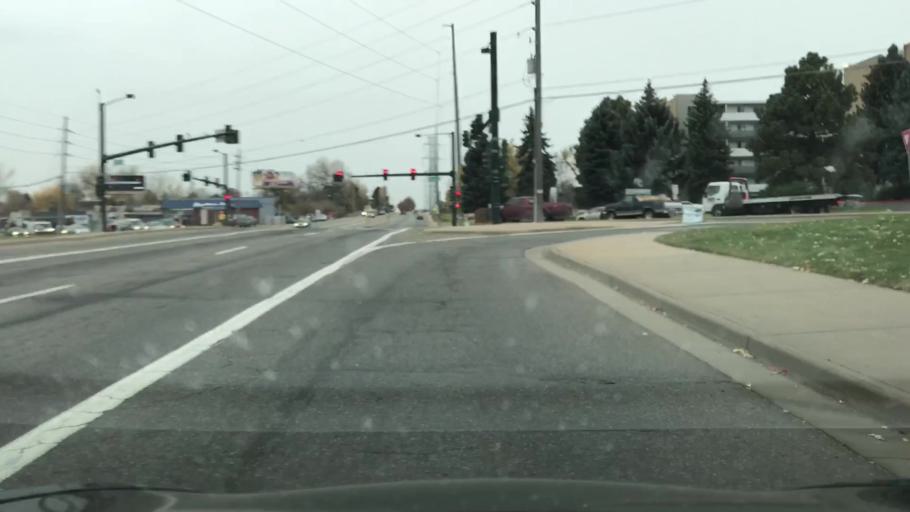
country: US
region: Colorado
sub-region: Arapahoe County
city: Glendale
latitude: 39.6774
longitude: -104.9038
